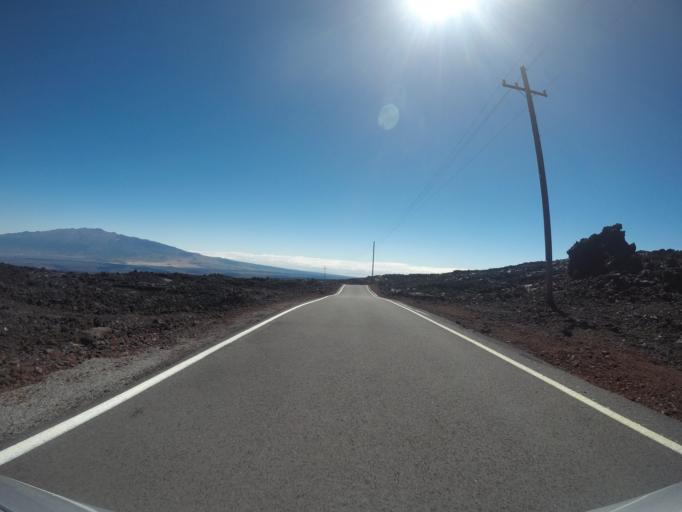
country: US
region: Hawaii
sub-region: Hawaii County
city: Volcano
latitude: 19.5539
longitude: -155.5377
